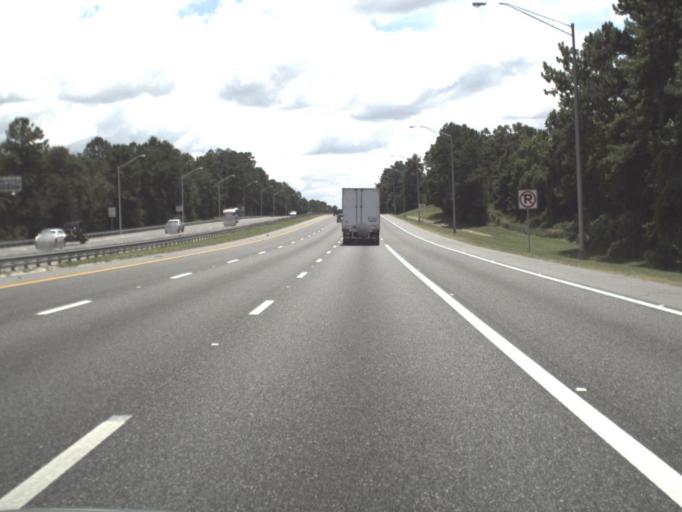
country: US
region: Florida
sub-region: Alachua County
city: High Springs
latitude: 29.9762
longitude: -82.5779
